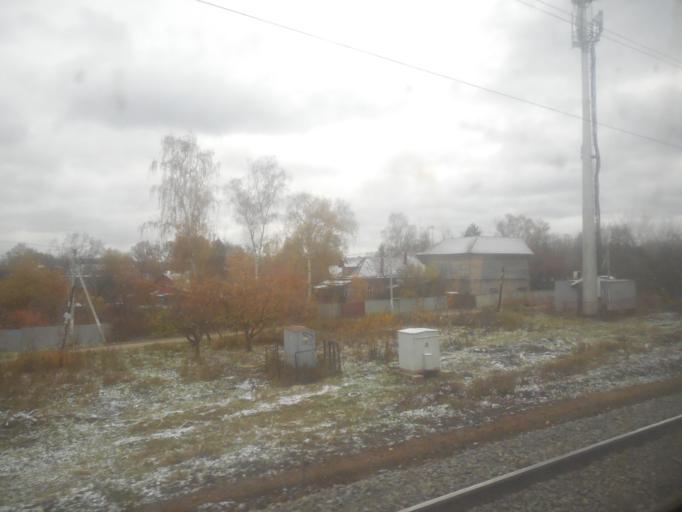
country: RU
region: Moscow
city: Novo-Peredelkino
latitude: 55.6841
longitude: 37.3203
